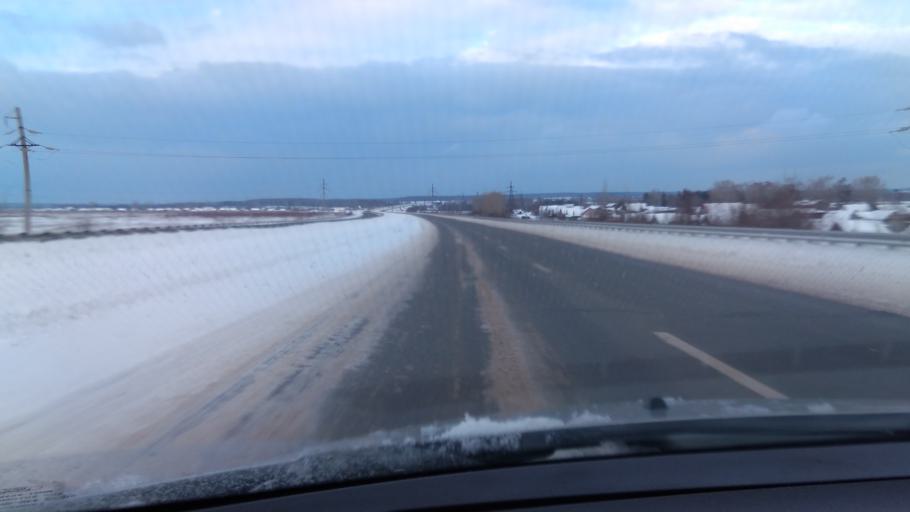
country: RU
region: Sverdlovsk
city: Tsementnyy
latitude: 57.4865
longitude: 60.1796
